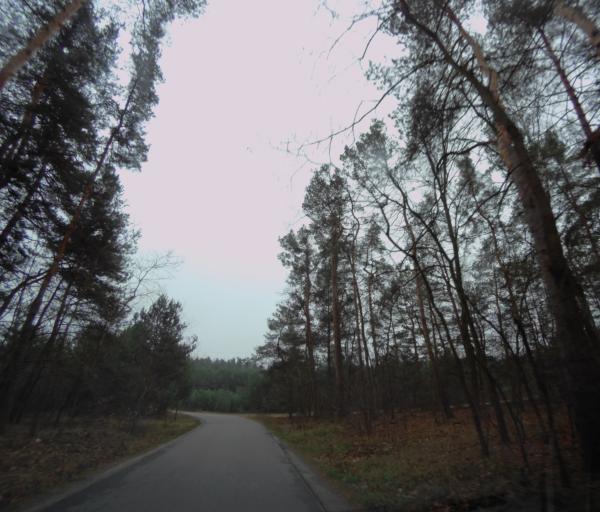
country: PL
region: Subcarpathian Voivodeship
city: Nowa Sarzyna
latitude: 50.3008
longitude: 22.3476
